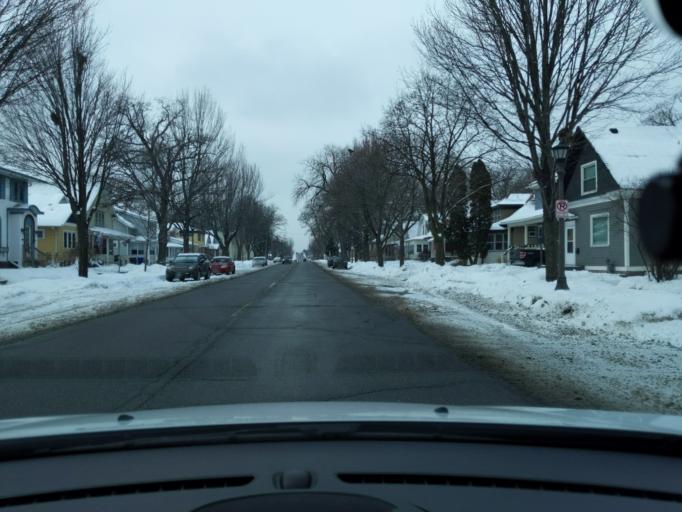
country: US
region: Minnesota
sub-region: Ramsey County
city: Falcon Heights
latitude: 44.9467
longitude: -93.1522
